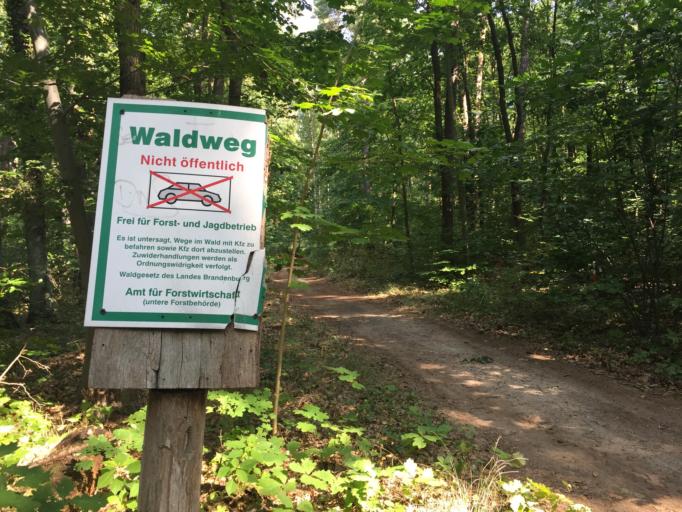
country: DE
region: Brandenburg
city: Michendorf
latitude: 52.3678
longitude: 13.0094
